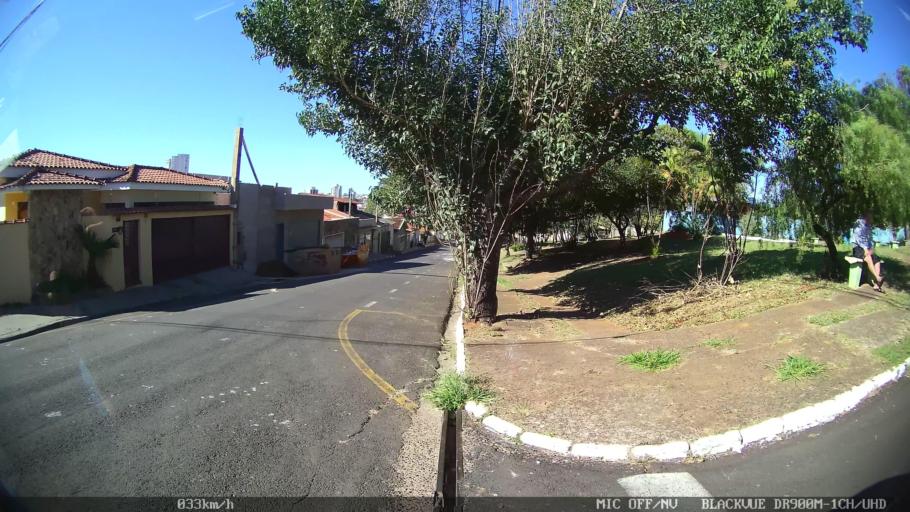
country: BR
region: Sao Paulo
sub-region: Franca
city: Franca
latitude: -20.5442
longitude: -47.4107
